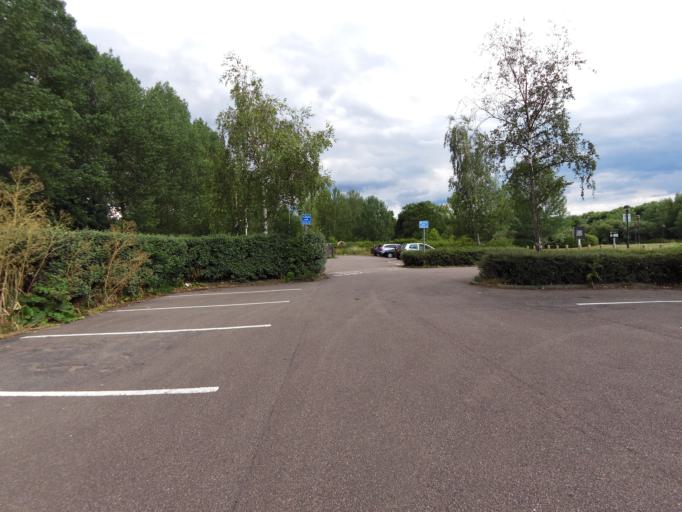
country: GB
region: England
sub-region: Hertfordshire
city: Broxbourne
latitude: 51.7438
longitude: -0.0095
